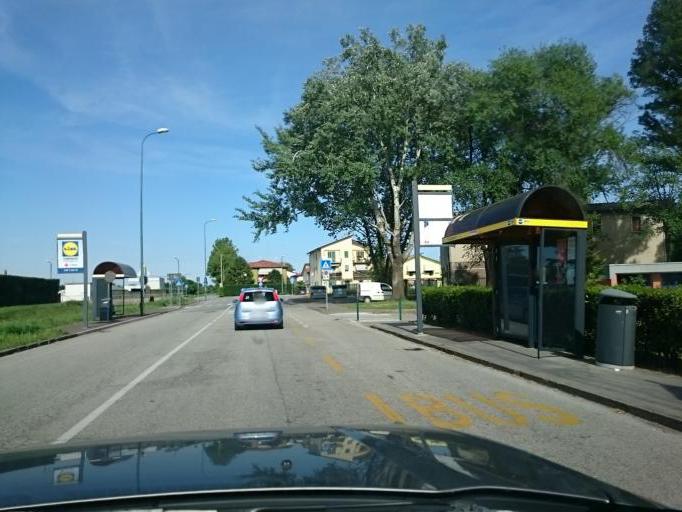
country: IT
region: Veneto
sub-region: Provincia di Venezia
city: Campalto
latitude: 45.4828
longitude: 12.2959
